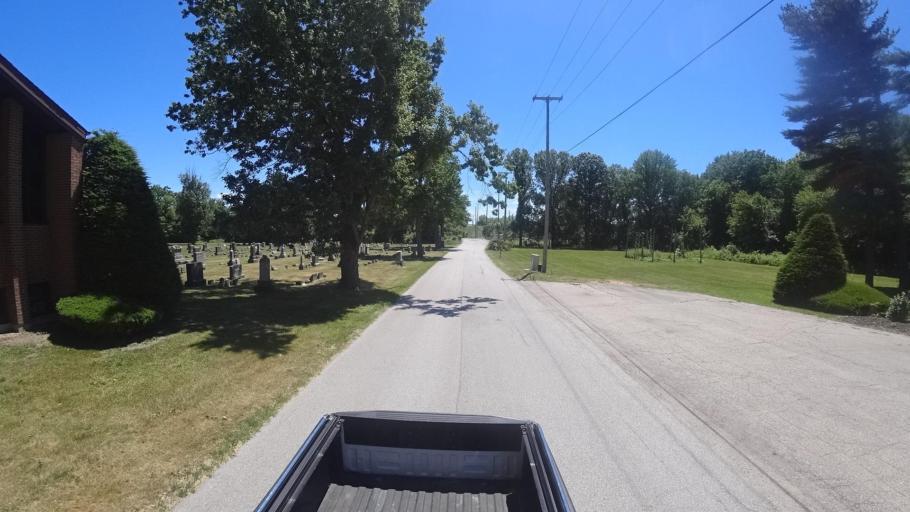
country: US
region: Indiana
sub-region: Porter County
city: Porter
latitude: 41.6159
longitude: -87.0868
